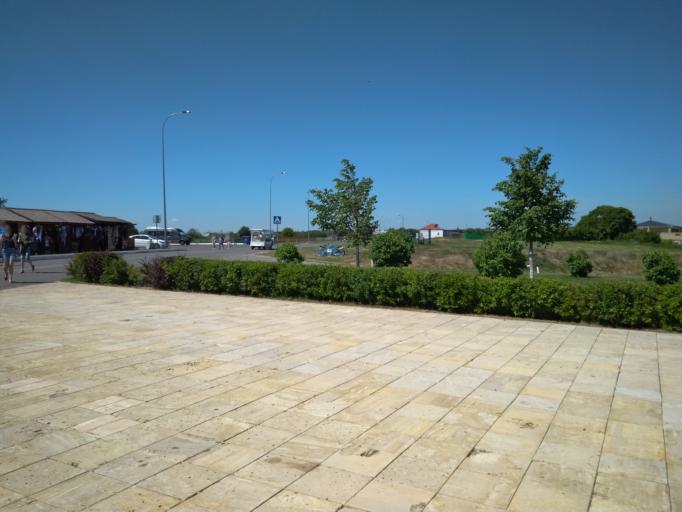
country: RU
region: Tatarstan
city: Bolgar
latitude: 54.9856
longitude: 49.0525
